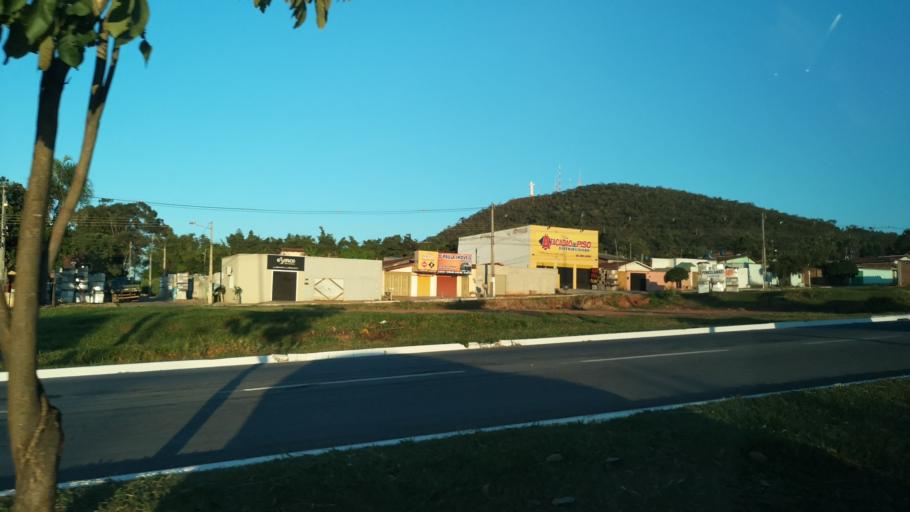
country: BR
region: Goias
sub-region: Senador Canedo
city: Senador Canedo
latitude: -16.6836
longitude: -49.1154
